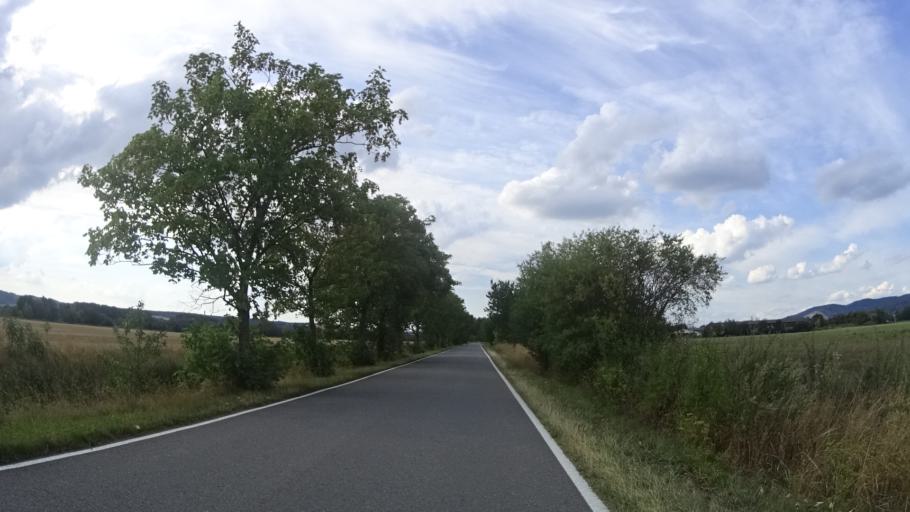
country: CZ
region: Olomoucky
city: Dubicko
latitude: 49.8188
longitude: 16.9398
